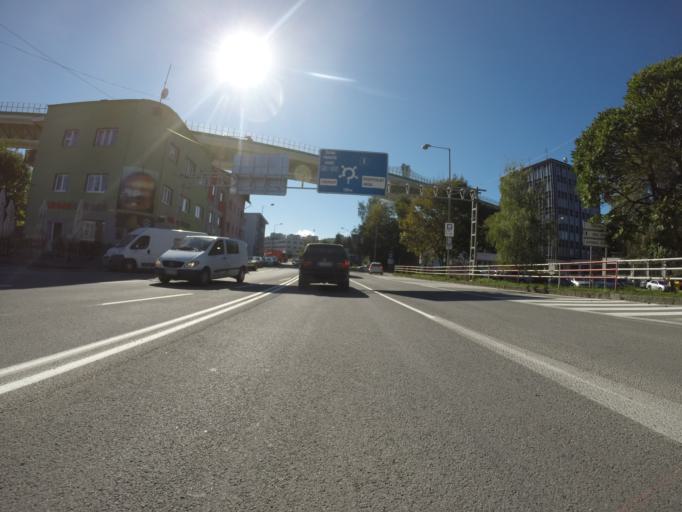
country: SK
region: Trenciansky
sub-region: Okres Povazska Bystrica
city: Povazska Bystrica
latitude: 49.1189
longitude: 18.4378
